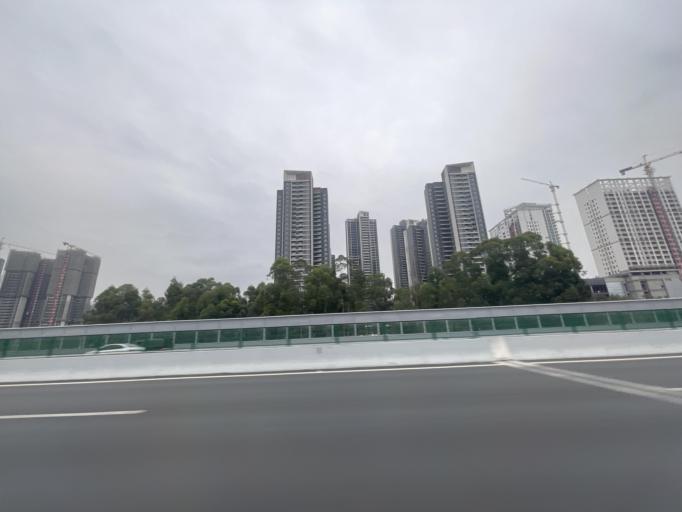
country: CN
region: Guangdong
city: Huangge
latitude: 22.7905
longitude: 113.5117
